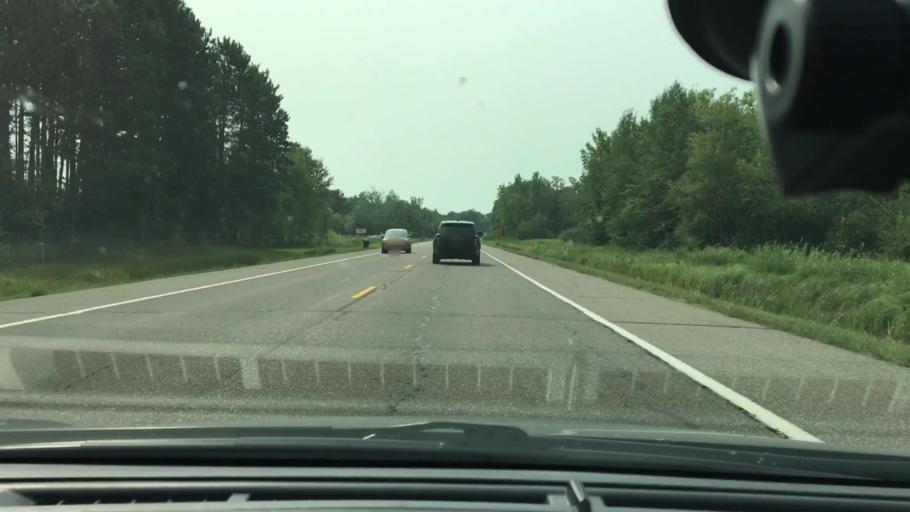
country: US
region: Minnesota
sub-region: Crow Wing County
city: Brainerd
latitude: 46.3897
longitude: -94.2233
